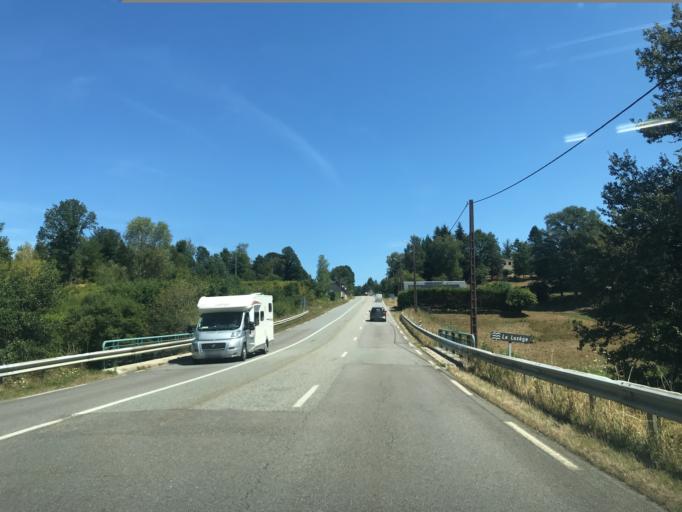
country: FR
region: Limousin
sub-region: Departement de la Correze
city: Meymac
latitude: 45.4685
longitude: 2.1509
